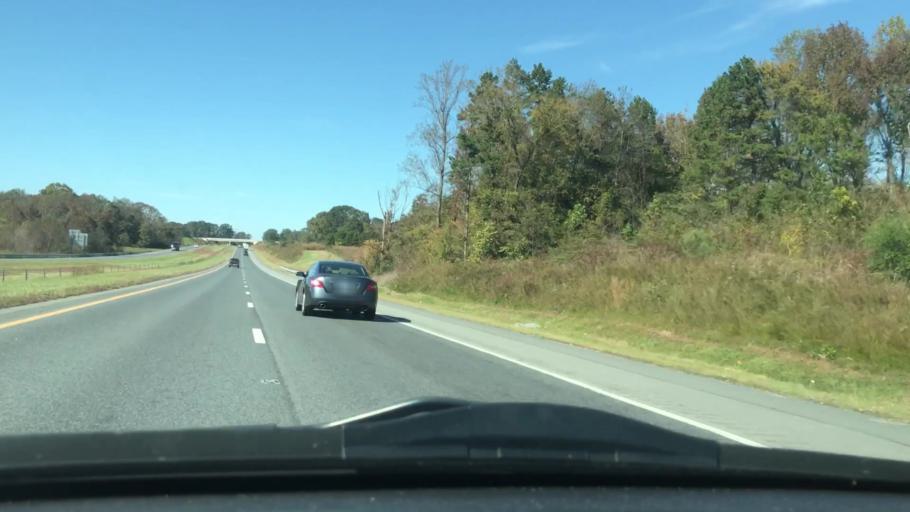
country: US
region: North Carolina
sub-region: Randolph County
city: Randleman
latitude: 35.8489
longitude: -79.8731
